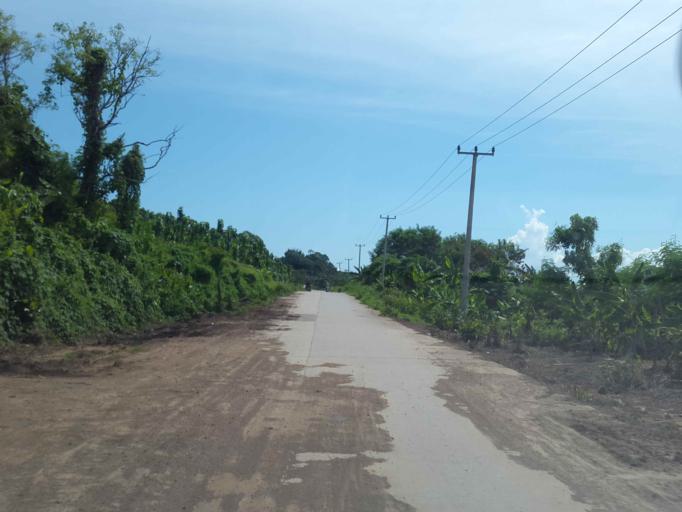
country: ID
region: Banten
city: Babakanbungur
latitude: -6.5215
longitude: 105.6301
